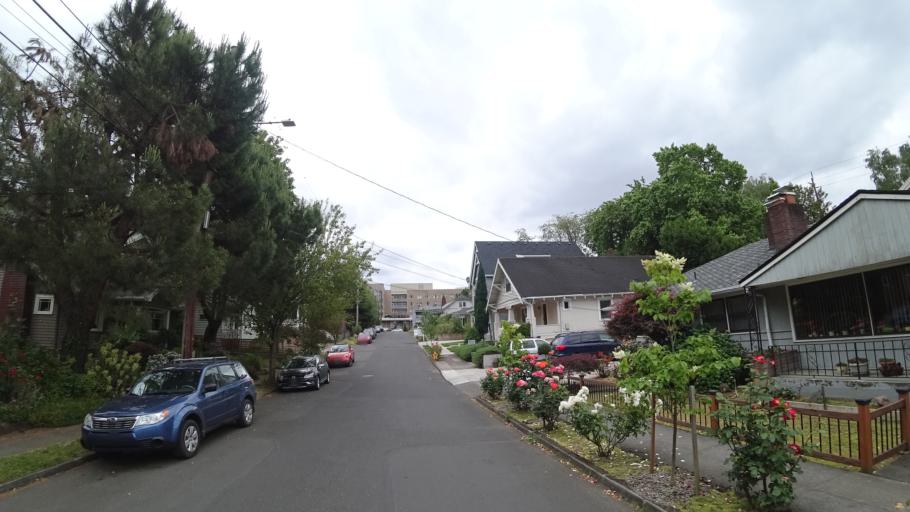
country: US
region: Oregon
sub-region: Multnomah County
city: Lents
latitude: 45.5179
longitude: -122.6012
